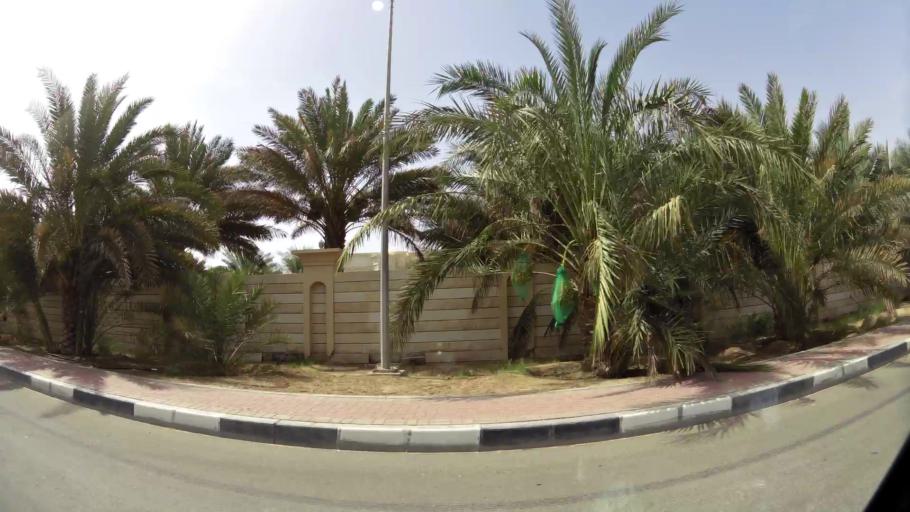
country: AE
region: Abu Dhabi
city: Al Ain
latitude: 24.1736
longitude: 55.6708
